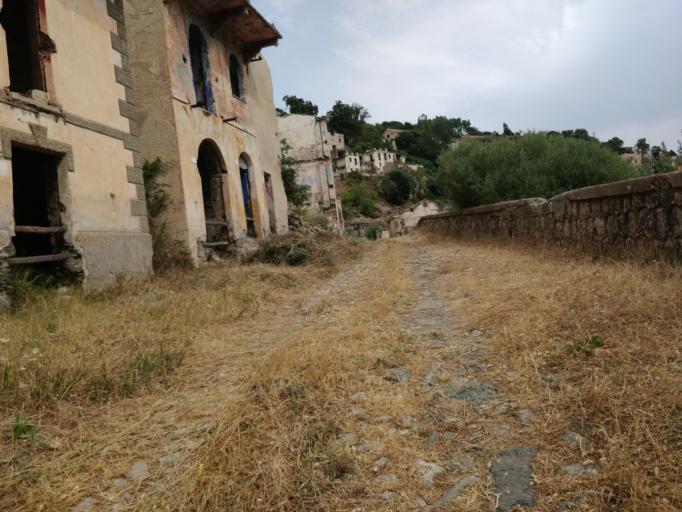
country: IT
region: Sardinia
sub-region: Provincia di Ogliastra
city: Gairo Sant'Elena
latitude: 39.8484
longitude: 9.4982
